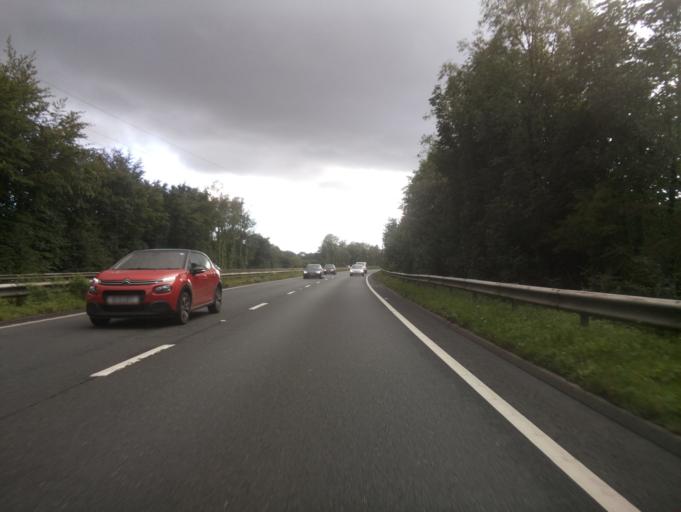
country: GB
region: England
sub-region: Devon
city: South Brent
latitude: 50.3955
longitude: -3.8694
